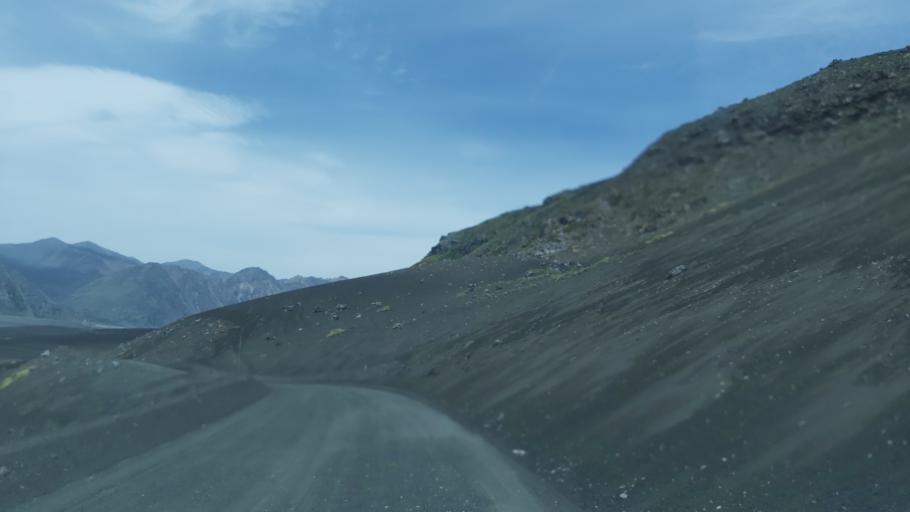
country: AR
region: Neuquen
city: Andacollo
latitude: -37.4066
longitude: -71.2997
